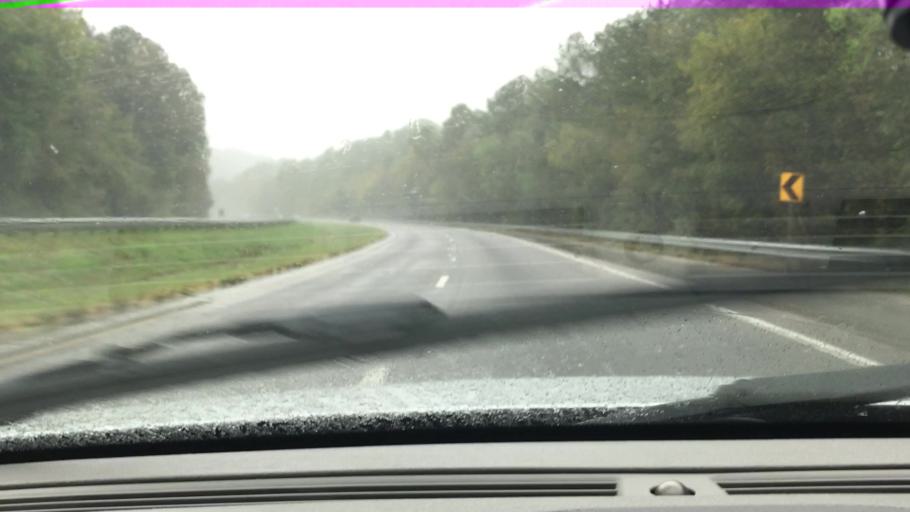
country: US
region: Alabama
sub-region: Limestone County
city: Ardmore
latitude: 34.9794
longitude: -86.8792
